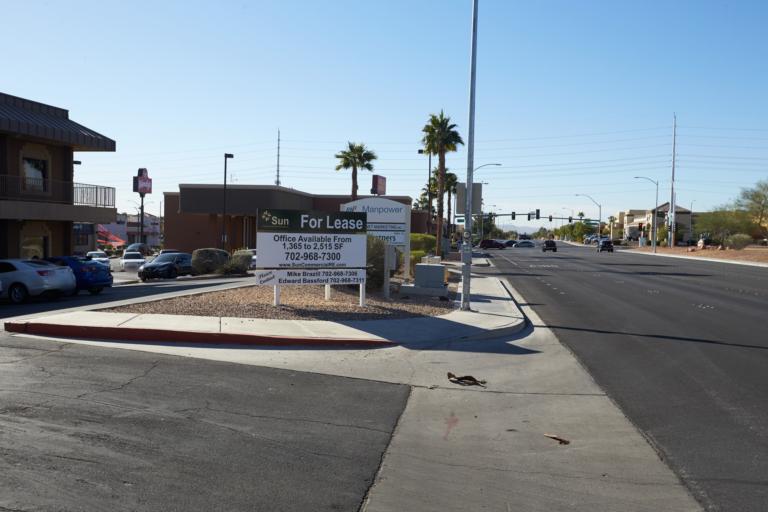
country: US
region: Nevada
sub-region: Clark County
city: Spring Valley
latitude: 36.1452
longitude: -115.2699
